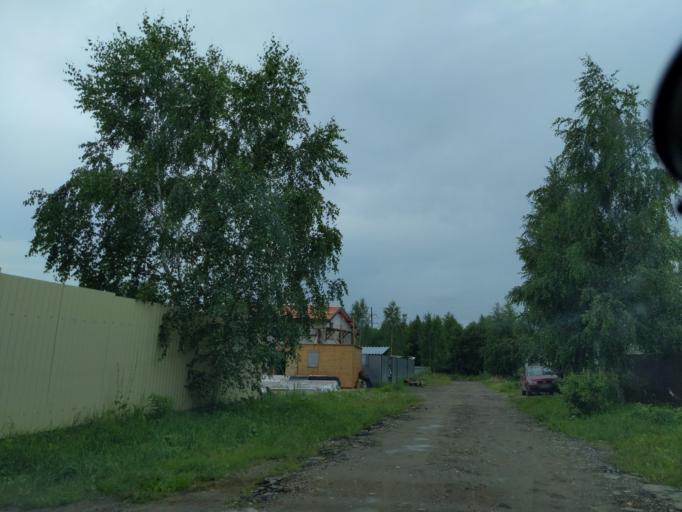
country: RU
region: Moskovskaya
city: Lugovaya
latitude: 56.0563
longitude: 37.4986
